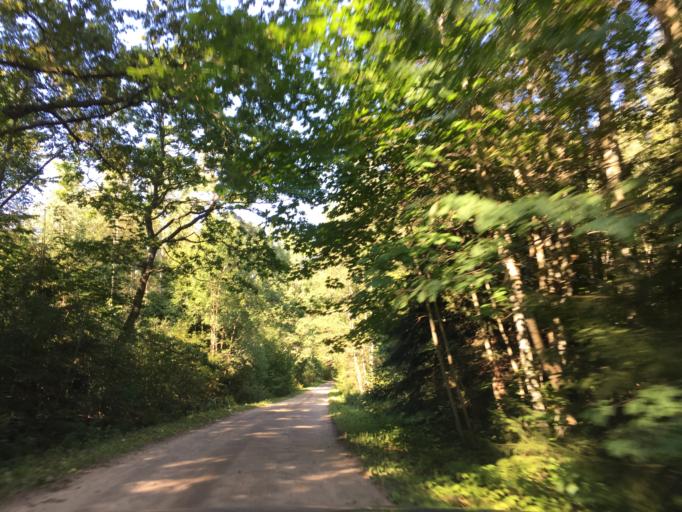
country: LV
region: Limbazu Rajons
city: Limbazi
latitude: 57.5551
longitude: 24.7814
